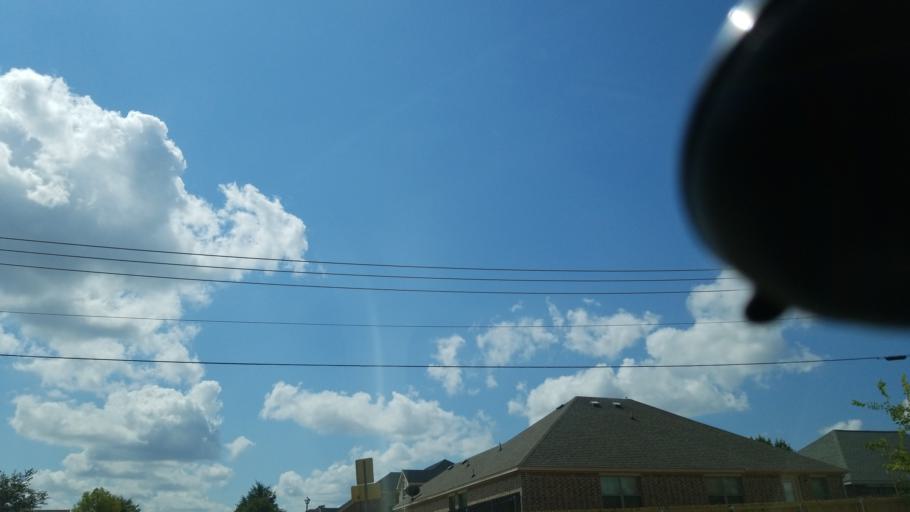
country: US
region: Texas
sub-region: Dallas County
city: Grand Prairie
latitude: 32.7257
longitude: -96.9884
